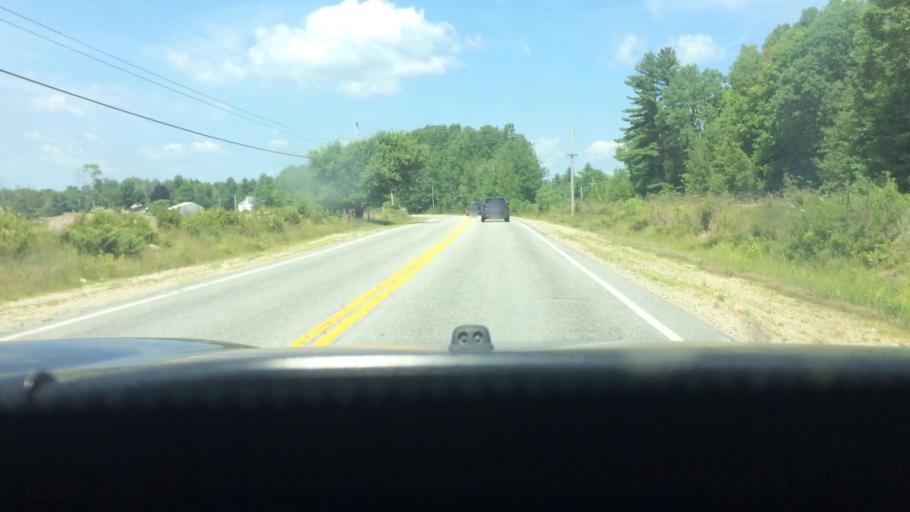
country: US
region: Maine
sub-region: Androscoggin County
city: Mechanic Falls
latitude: 44.1309
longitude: -70.4390
